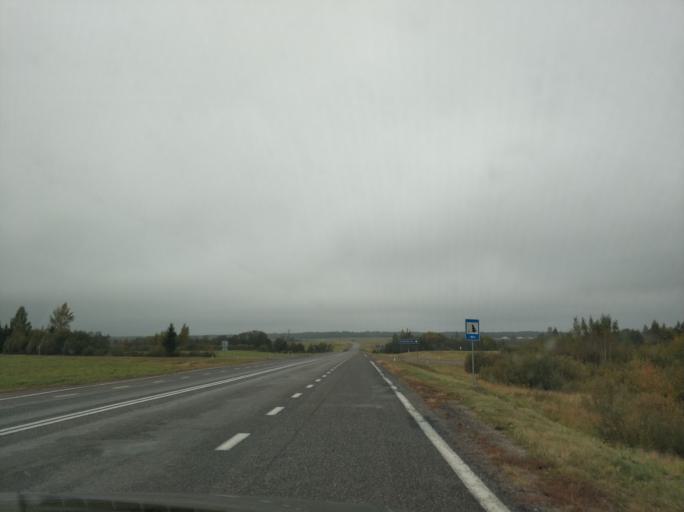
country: BY
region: Vitebsk
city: Chashniki
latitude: 55.3544
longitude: 29.3449
